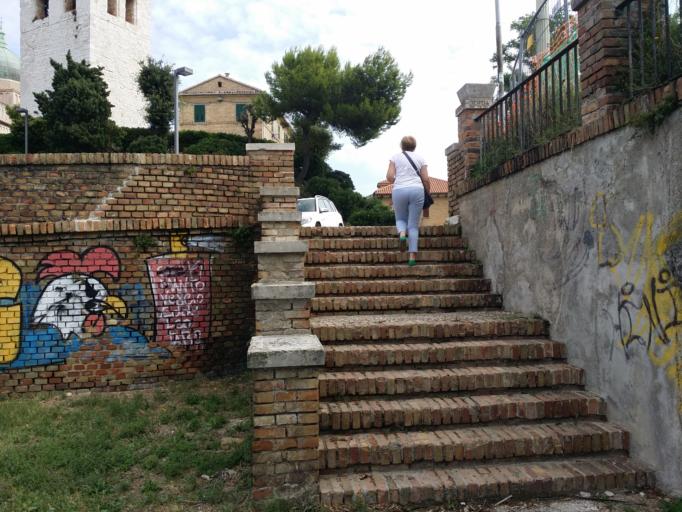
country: IT
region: The Marches
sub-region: Provincia di Ancona
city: Le Grazie di Ancona
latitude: 43.6243
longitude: 13.5100
